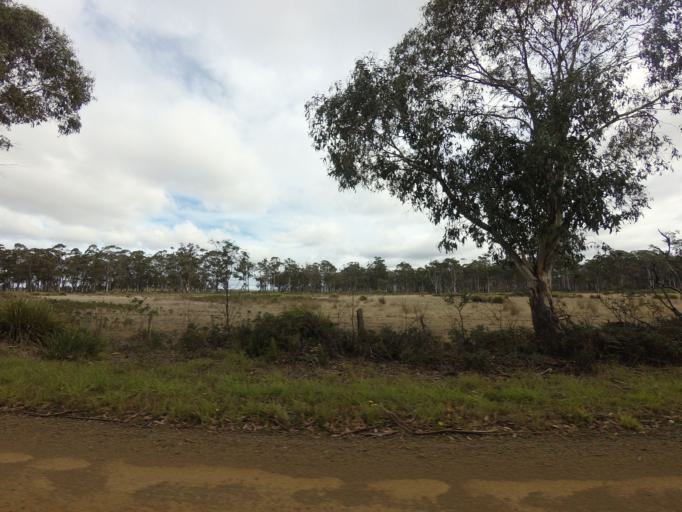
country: AU
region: Tasmania
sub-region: Brighton
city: Bridgewater
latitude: -42.4224
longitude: 147.4238
